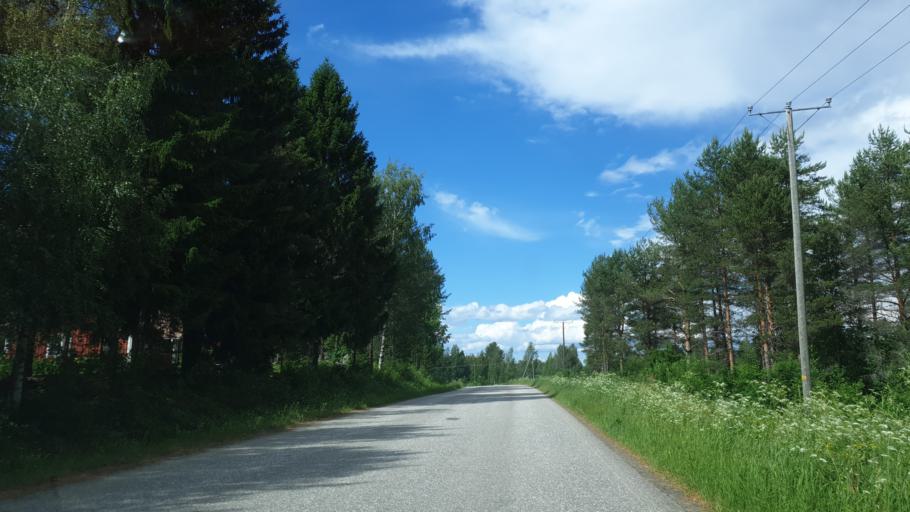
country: FI
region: Northern Savo
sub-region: Koillis-Savo
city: Kaavi
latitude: 62.9972
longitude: 28.7168
